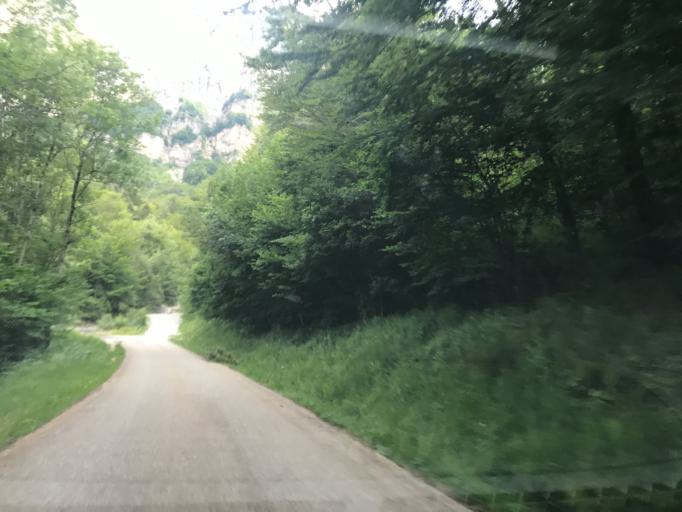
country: FR
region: Rhone-Alpes
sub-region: Departement de l'Isere
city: Saint-Vincent-de-Mercuze
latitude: 45.3803
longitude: 5.9235
